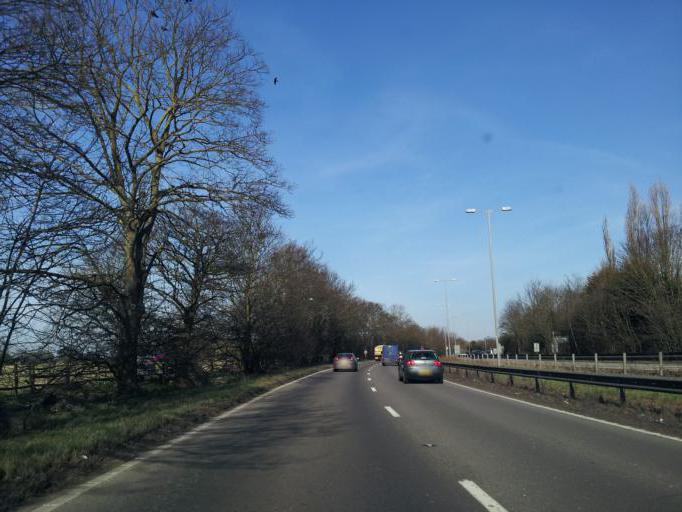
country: GB
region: England
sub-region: Cambridgeshire
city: Buckden
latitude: 52.2940
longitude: -0.2563
